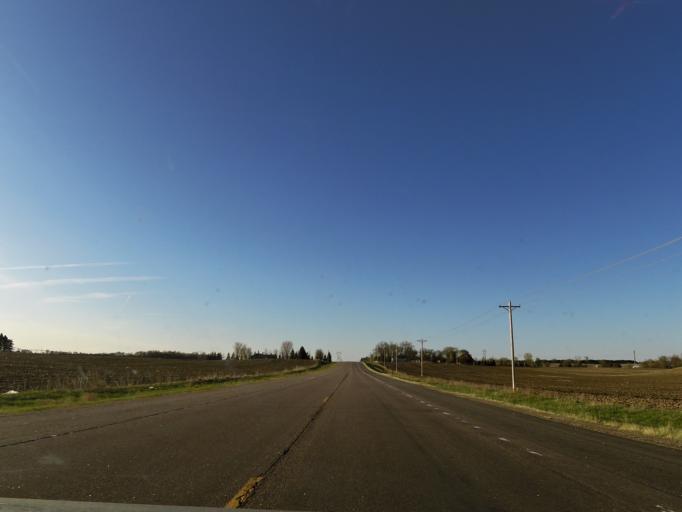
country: US
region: Wisconsin
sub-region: Pierce County
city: Prescott
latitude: 44.6185
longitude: -92.7726
